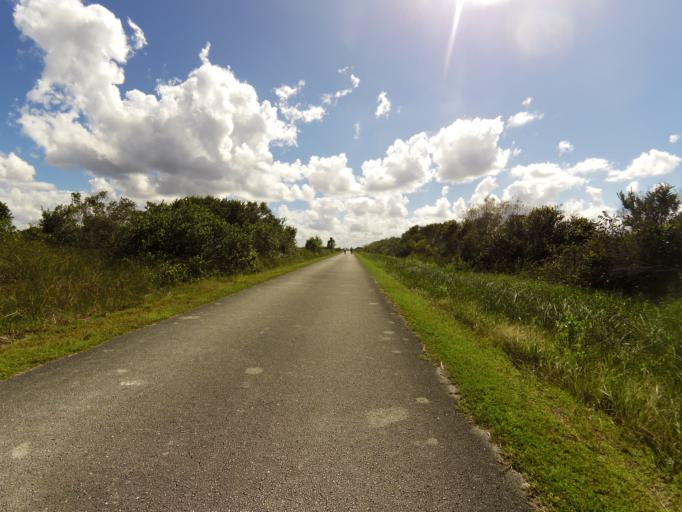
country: US
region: Florida
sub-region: Miami-Dade County
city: The Hammocks
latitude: 25.7049
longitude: -80.7668
